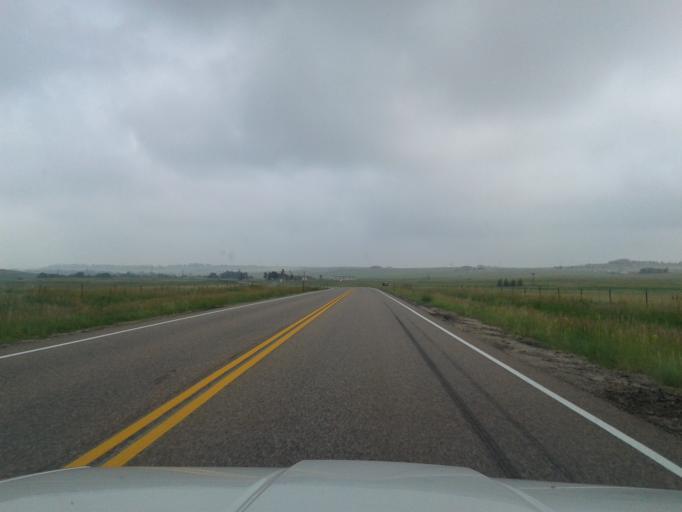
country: US
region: Colorado
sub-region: Elbert County
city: Elizabeth
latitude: 39.2225
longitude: -104.7013
